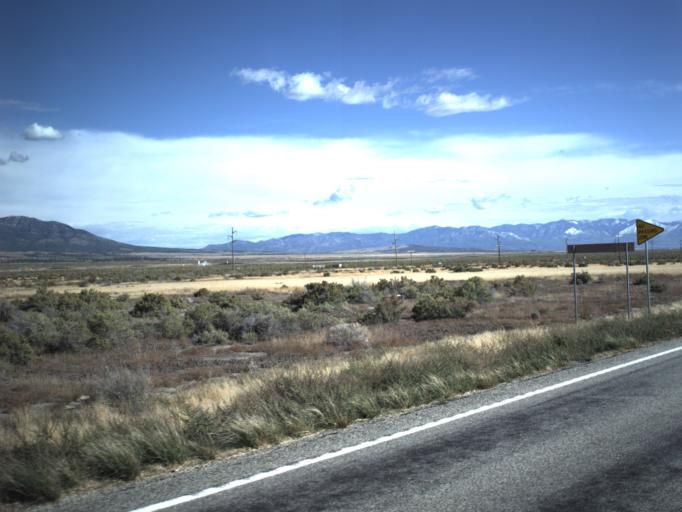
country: US
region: Utah
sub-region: Millard County
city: Delta
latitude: 39.2907
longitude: -112.4661
